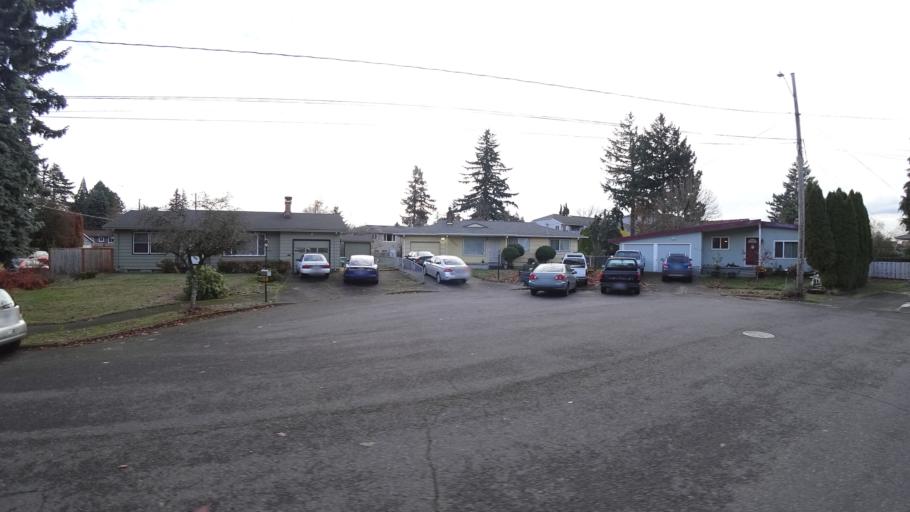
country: US
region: Oregon
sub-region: Multnomah County
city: Lents
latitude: 45.5176
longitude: -122.5320
